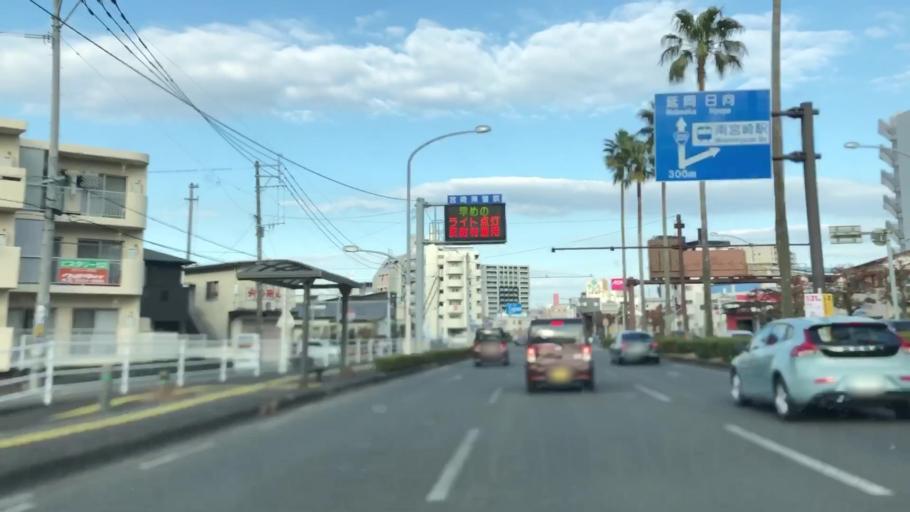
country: JP
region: Miyazaki
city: Miyazaki-shi
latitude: 31.8909
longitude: 131.4140
